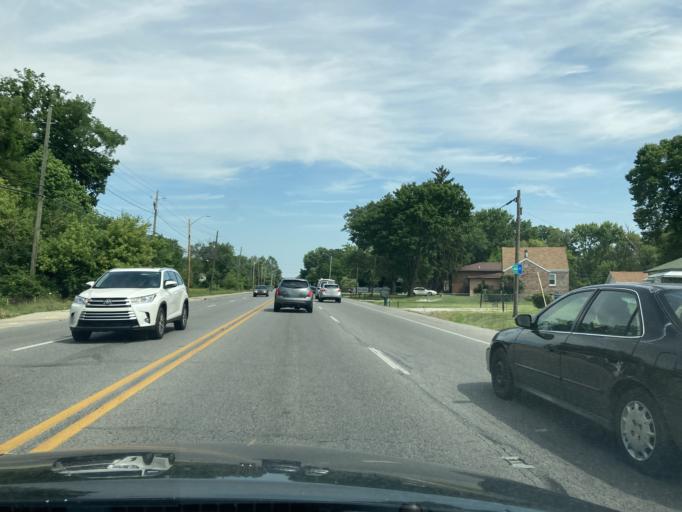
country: US
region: Indiana
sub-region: Marion County
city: Meridian Hills
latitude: 39.8693
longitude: -86.2023
